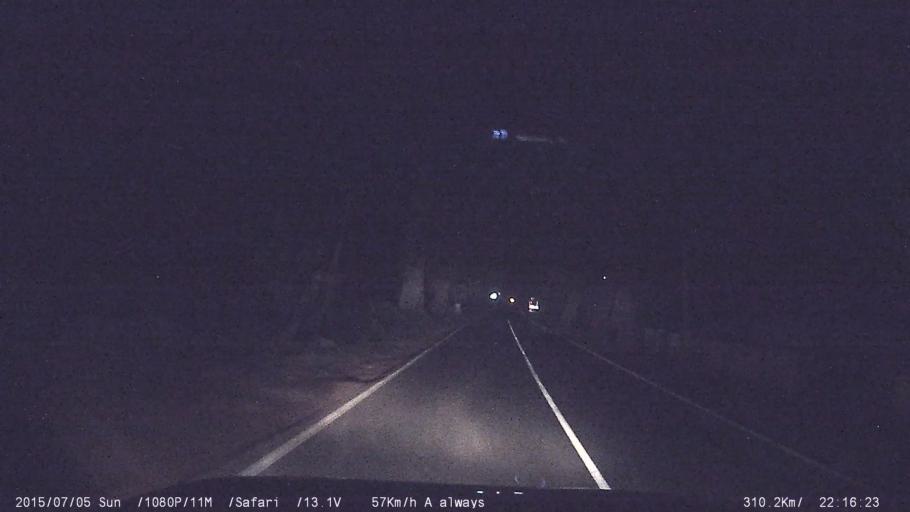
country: IN
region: Kerala
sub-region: Palakkad district
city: Palakkad
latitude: 10.8607
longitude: 76.5642
